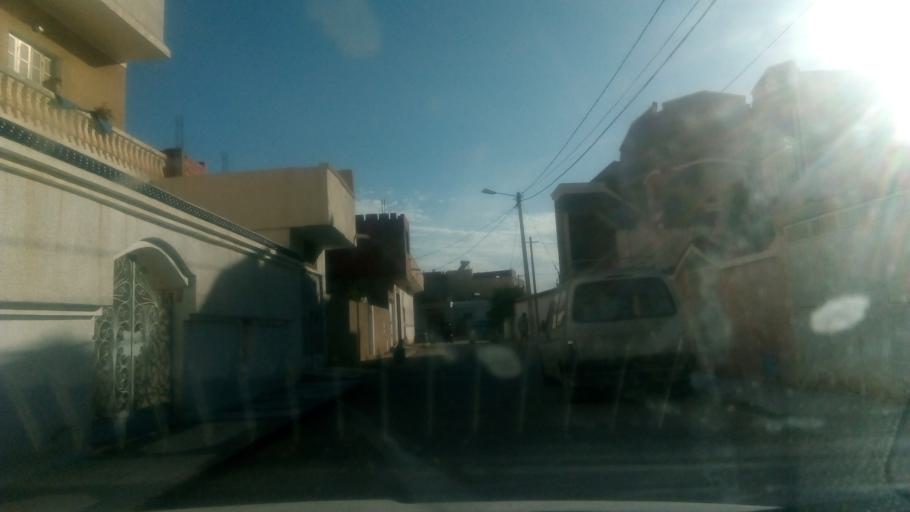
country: TN
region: Al Qayrawan
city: Kairouan
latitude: 35.6670
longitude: 10.0788
